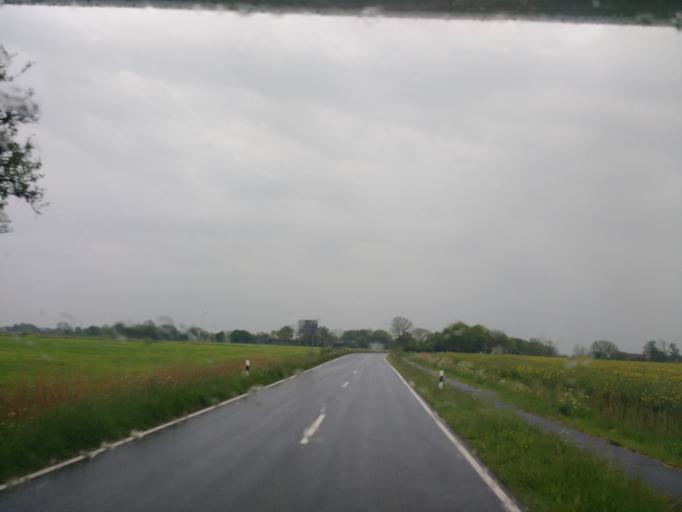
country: DE
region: Lower Saxony
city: Wangerooge
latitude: 53.6917
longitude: 7.9033
